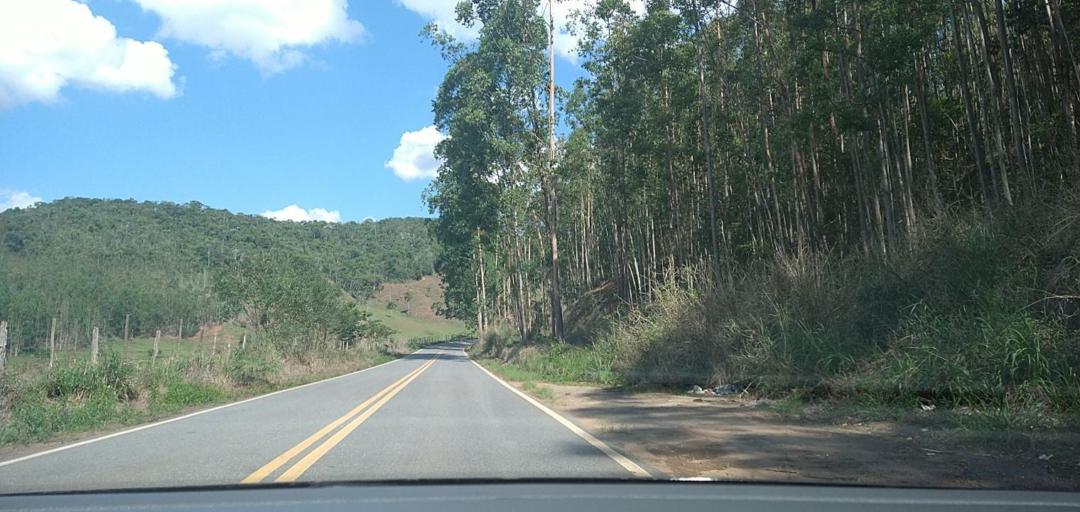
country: BR
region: Minas Gerais
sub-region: Rio Piracicaba
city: Rio Piracicaba
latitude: -19.9808
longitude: -43.1248
